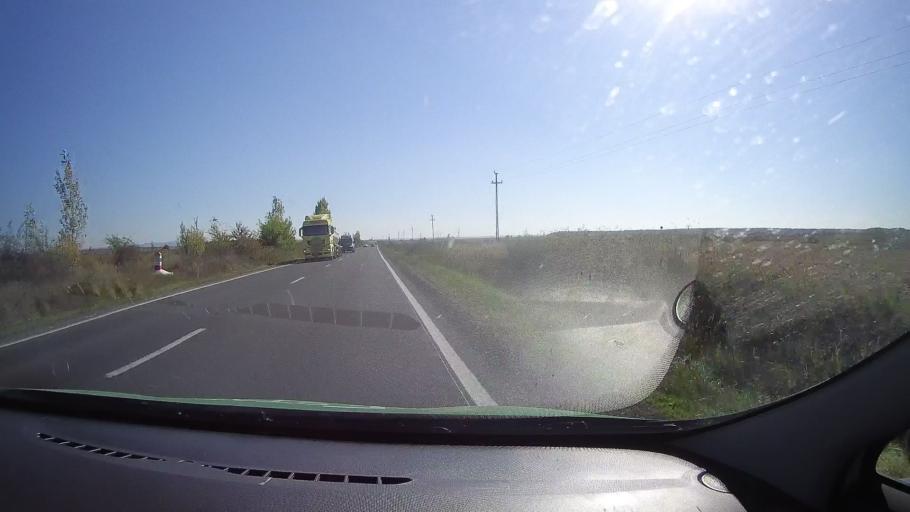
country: RO
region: Satu Mare
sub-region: Oras Ardud
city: Madaras
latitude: 47.6610
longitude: 22.8732
